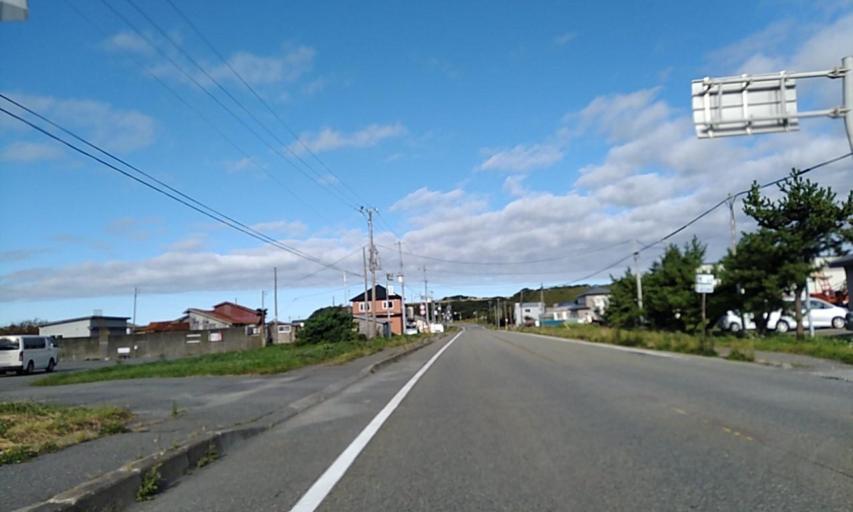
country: JP
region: Hokkaido
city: Shizunai-furukawacho
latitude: 42.2456
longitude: 142.5785
